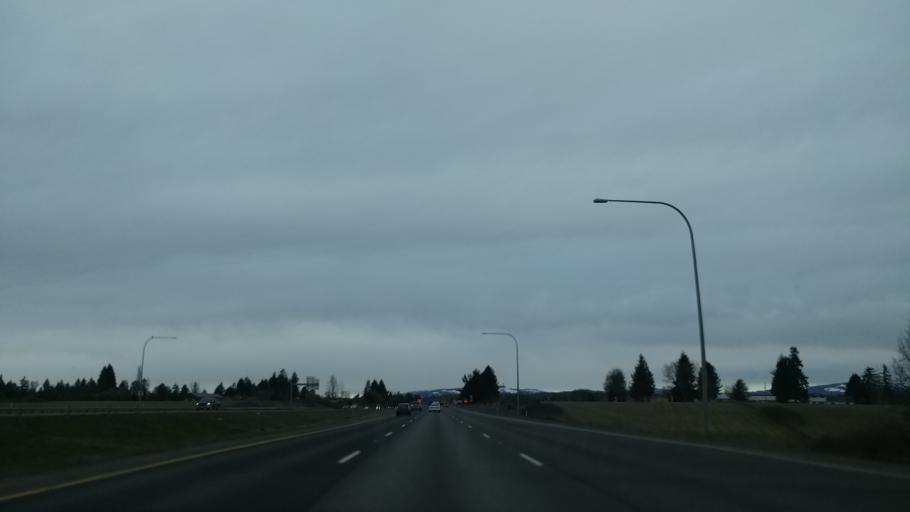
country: US
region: Washington
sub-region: Clark County
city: La Center
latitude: 45.8198
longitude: -122.6877
